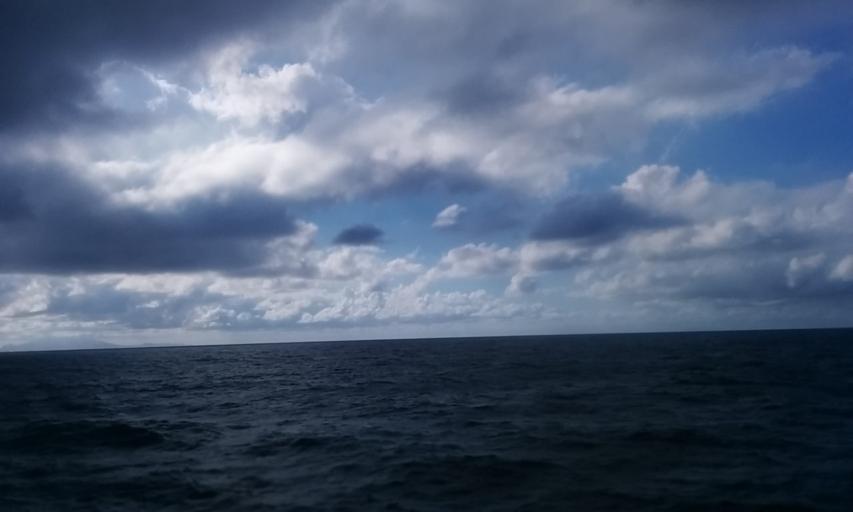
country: JP
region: Kagoshima
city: Nishinoomote
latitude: 30.5807
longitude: 130.5942
